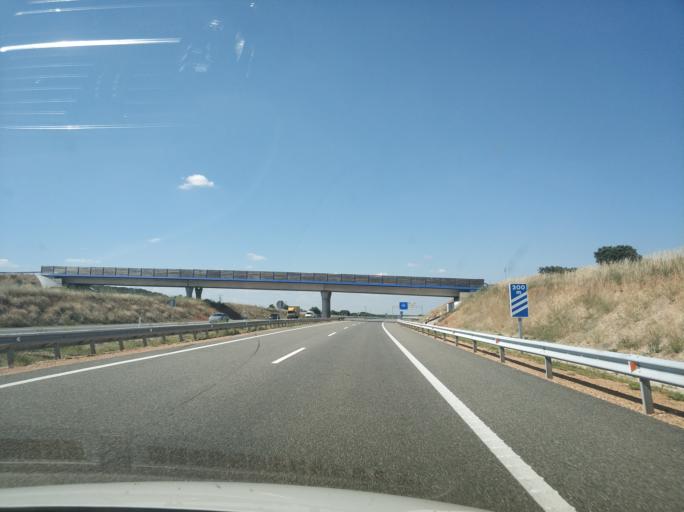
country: ES
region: Castille and Leon
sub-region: Provincia de Zamora
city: Montamarta
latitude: 41.6811
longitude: -5.8052
